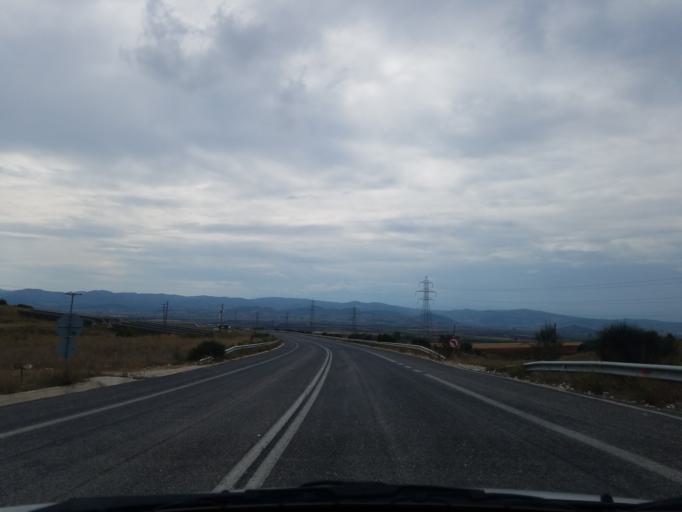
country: GR
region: Central Greece
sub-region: Nomos Fthiotidos
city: Domokos
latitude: 39.0955
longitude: 22.3046
